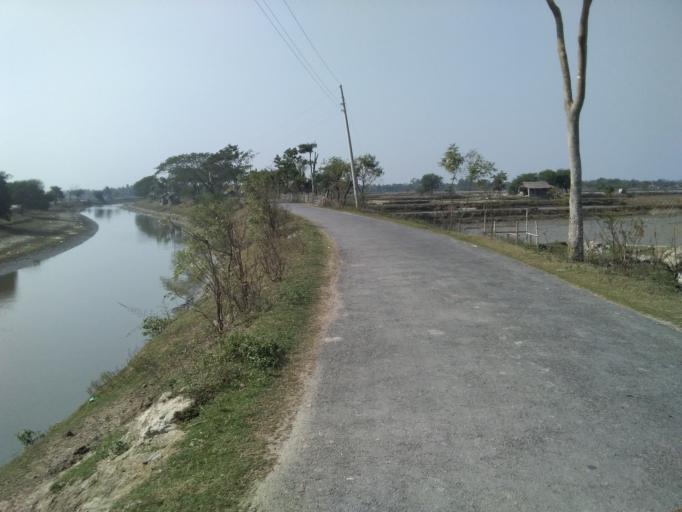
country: IN
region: West Bengal
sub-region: North 24 Parganas
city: Taki
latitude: 22.6353
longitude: 89.0079
